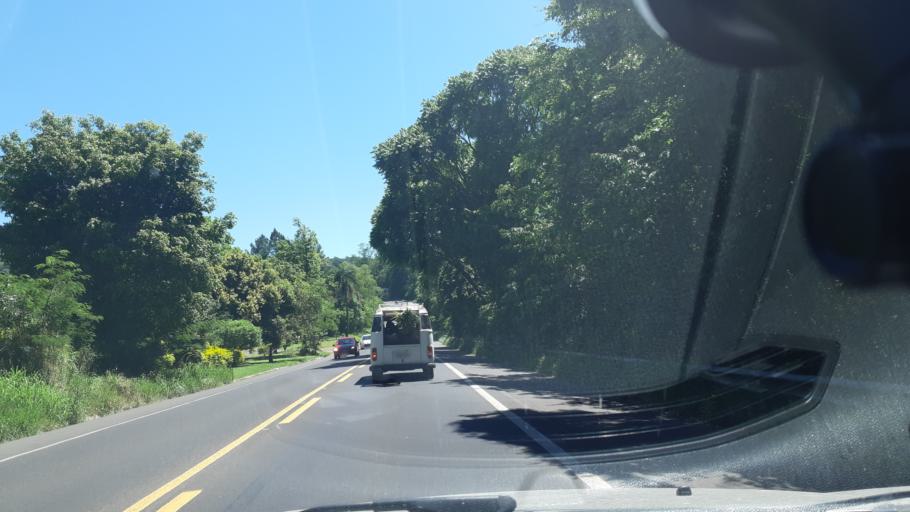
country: BR
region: Rio Grande do Sul
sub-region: Estancia Velha
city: Estancia Velha
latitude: -29.6414
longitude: -51.1426
